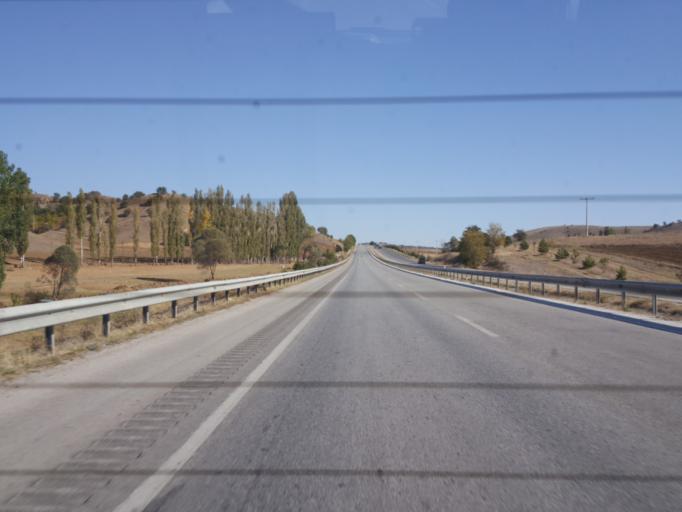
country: TR
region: Corum
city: Alaca
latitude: 40.2816
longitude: 34.6458
